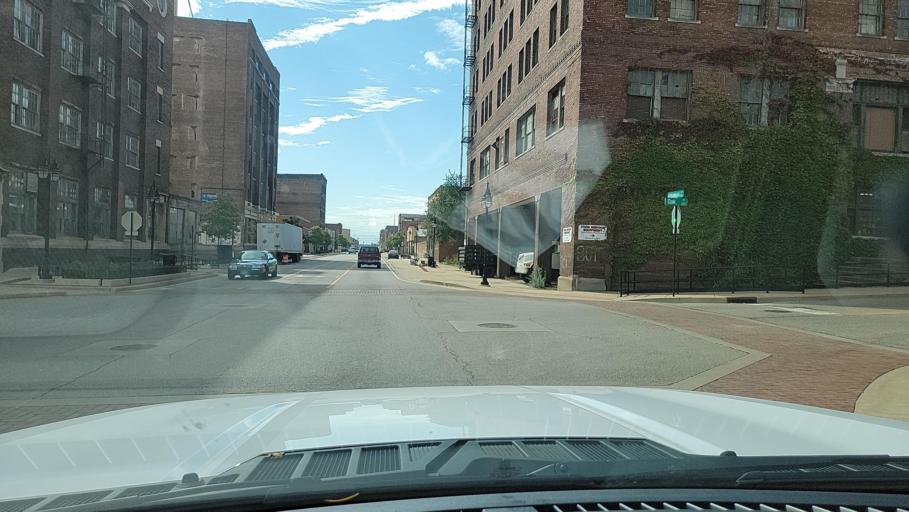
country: US
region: Illinois
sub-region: Peoria County
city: Peoria
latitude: 40.6854
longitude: -89.5971
